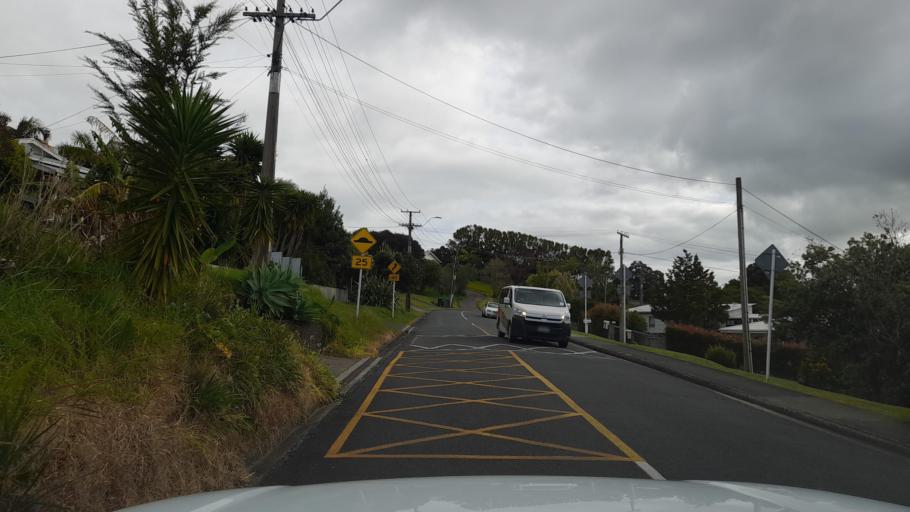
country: NZ
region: Northland
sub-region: Whangarei
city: Whangarei
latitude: -35.7374
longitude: 174.3267
